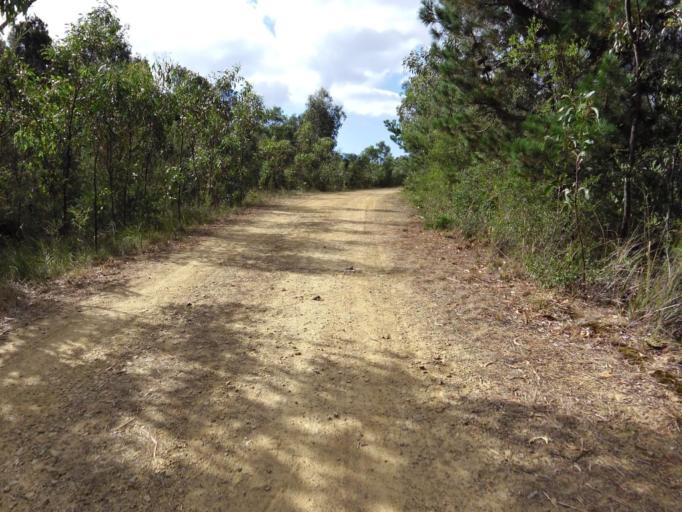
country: AU
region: Victoria
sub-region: Frankston
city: Frankston South
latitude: -38.1759
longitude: 145.1272
